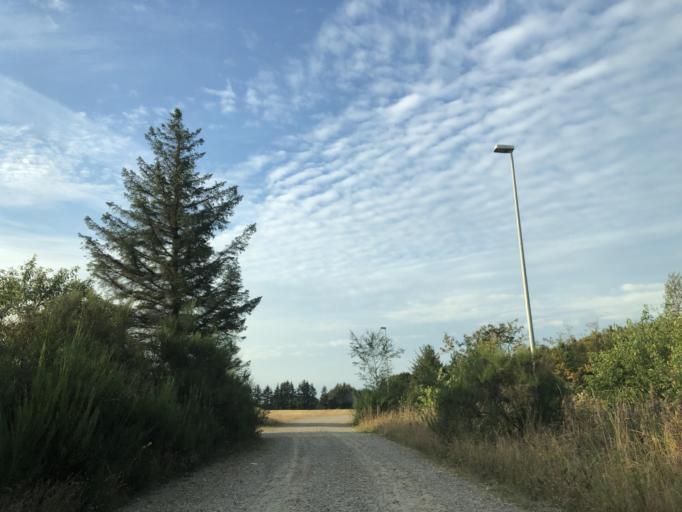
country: DK
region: Central Jutland
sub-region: Holstebro Kommune
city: Ulfborg
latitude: 56.2597
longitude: 8.3215
